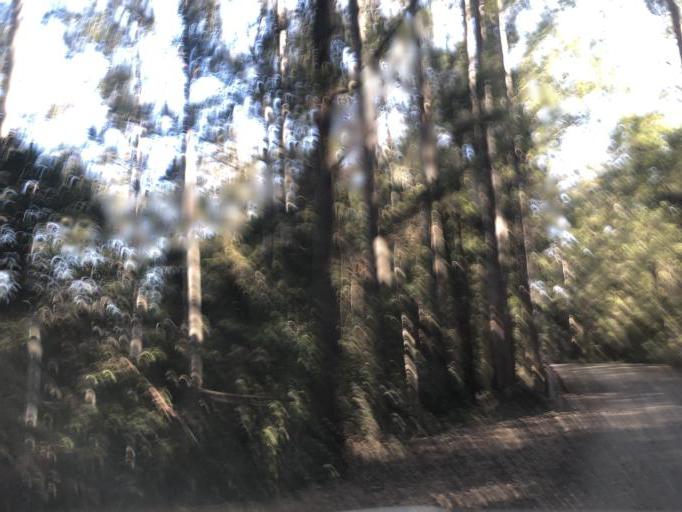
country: AU
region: New South Wales
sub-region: Bellingen
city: Bellingen
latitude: -30.4335
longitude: 152.8386
